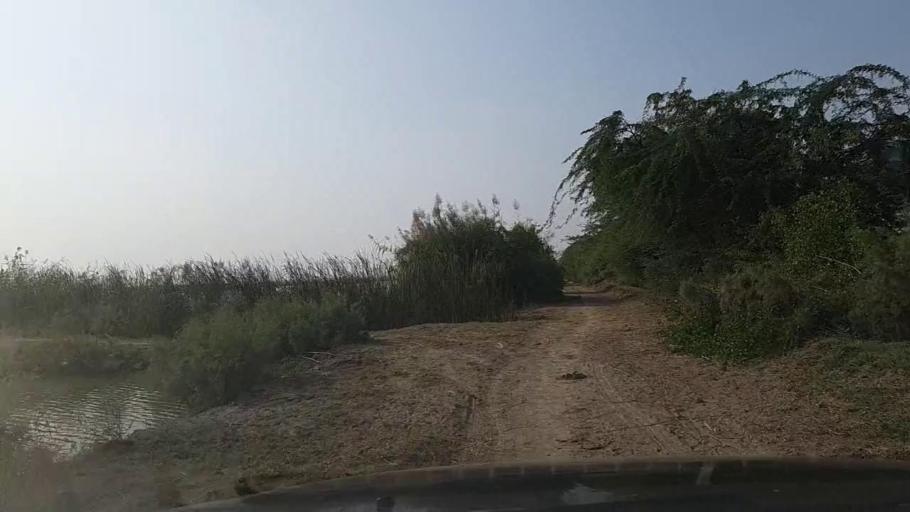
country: PK
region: Sindh
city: Mirpur Batoro
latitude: 24.6487
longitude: 68.2764
